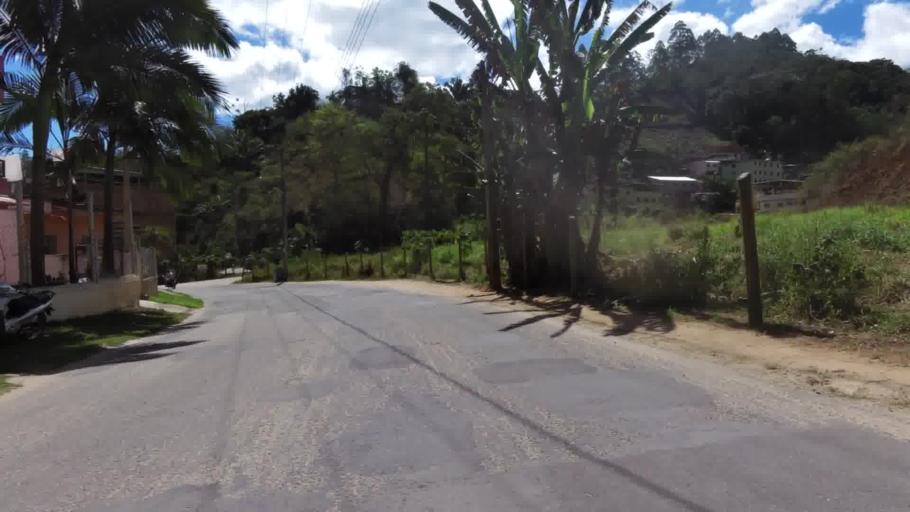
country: BR
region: Espirito Santo
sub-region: Vargem Alta
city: Vargem Alta
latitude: -20.6721
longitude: -41.0036
